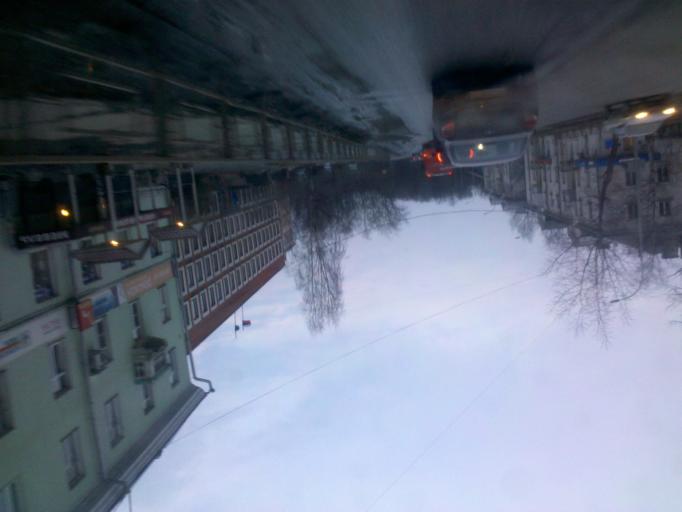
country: RU
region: Republic of Karelia
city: Petrozavodsk
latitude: 61.7820
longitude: 34.3863
